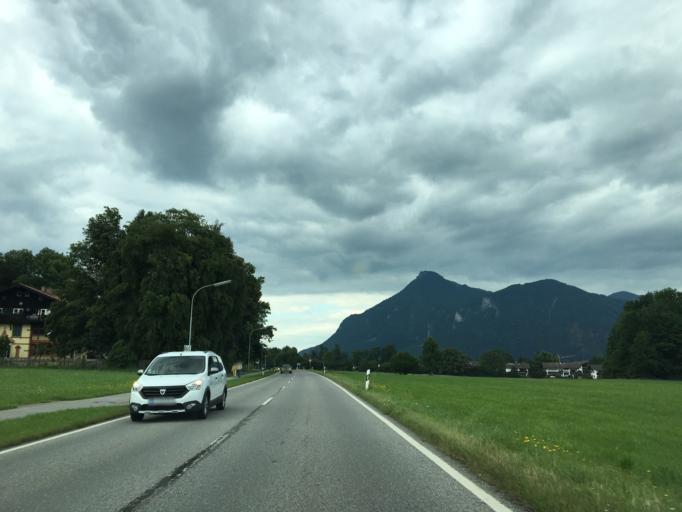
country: DE
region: Bavaria
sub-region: Upper Bavaria
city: Oberaudorf
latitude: 47.6541
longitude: 12.1728
